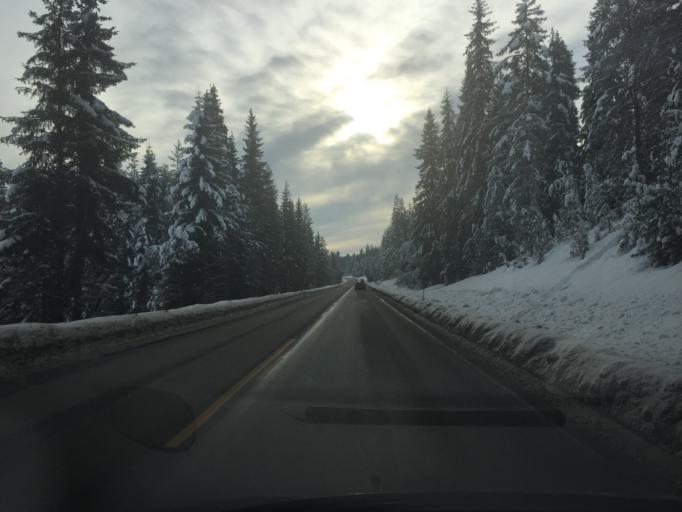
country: NO
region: Hedmark
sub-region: Trysil
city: Innbygda
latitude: 61.2842
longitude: 12.2817
